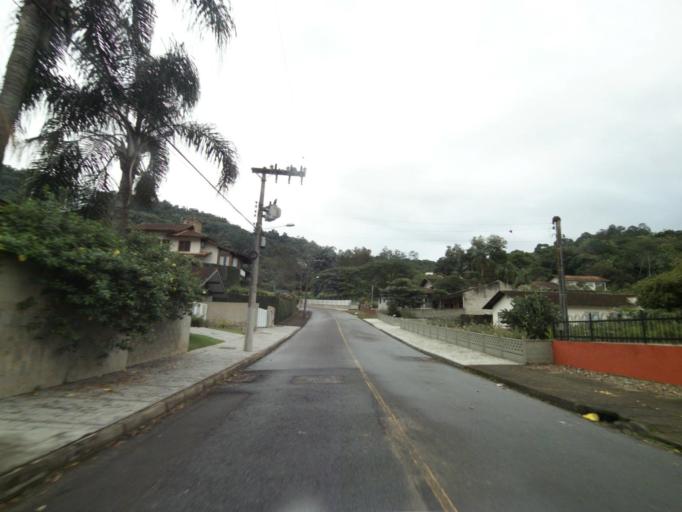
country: BR
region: Santa Catarina
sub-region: Pomerode
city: Pomerode
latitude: -26.7336
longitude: -49.1804
